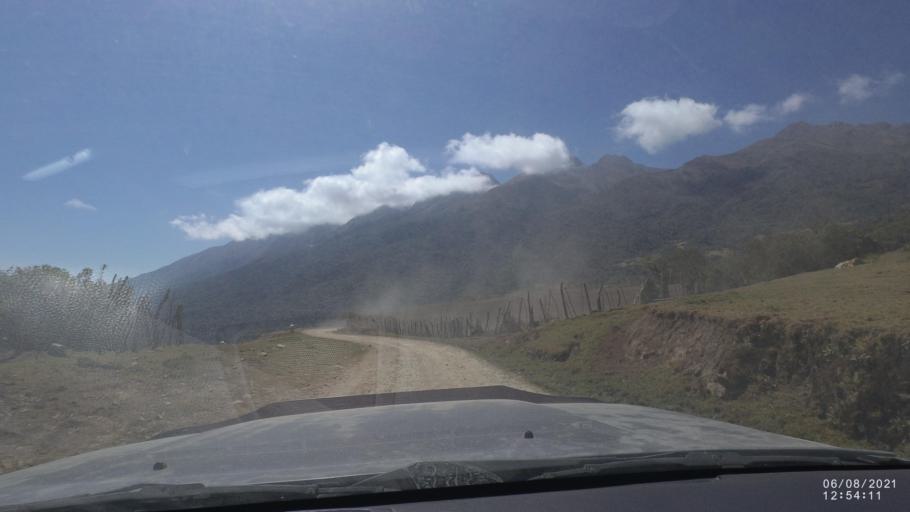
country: BO
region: Cochabamba
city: Colchani
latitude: -16.7592
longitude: -66.6837
